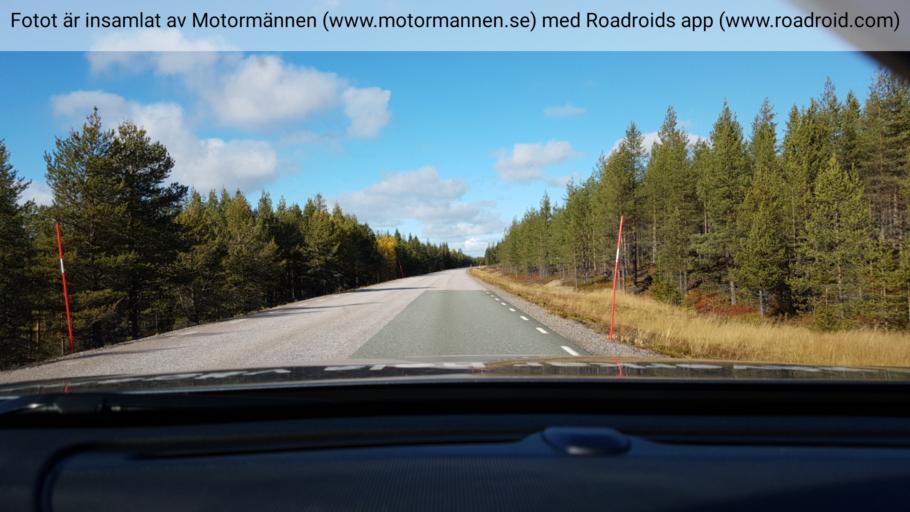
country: SE
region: Norrbotten
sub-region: Arvidsjaurs Kommun
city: Arvidsjaur
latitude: 65.7313
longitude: 18.6467
